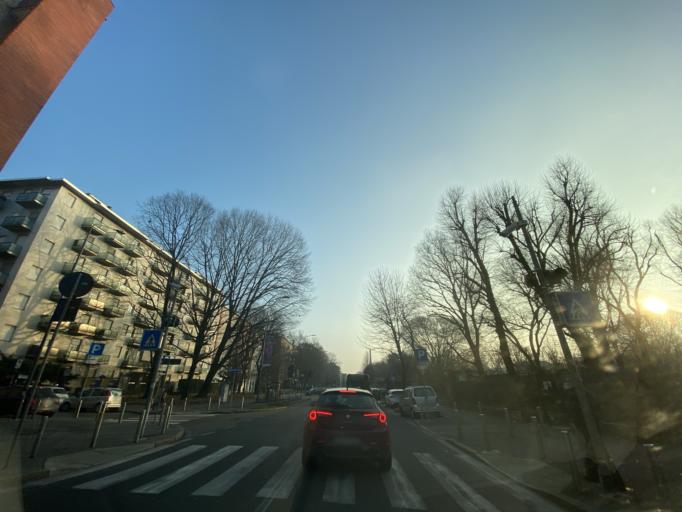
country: IT
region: Lombardy
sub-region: Citta metropolitana di Milano
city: Milano
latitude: 45.5004
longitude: 9.1783
